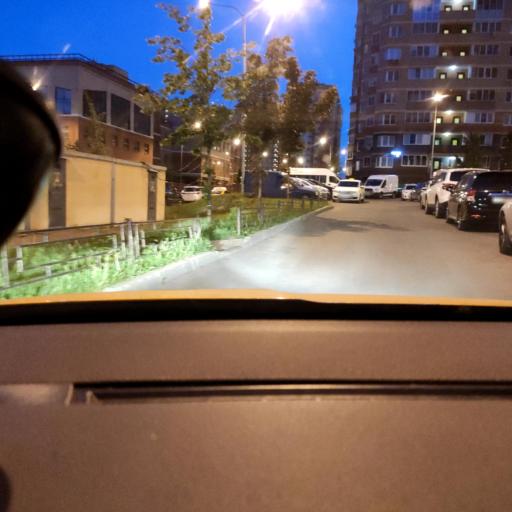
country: RU
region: Moskovskaya
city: Vidnoye
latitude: 55.5574
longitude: 37.6978
